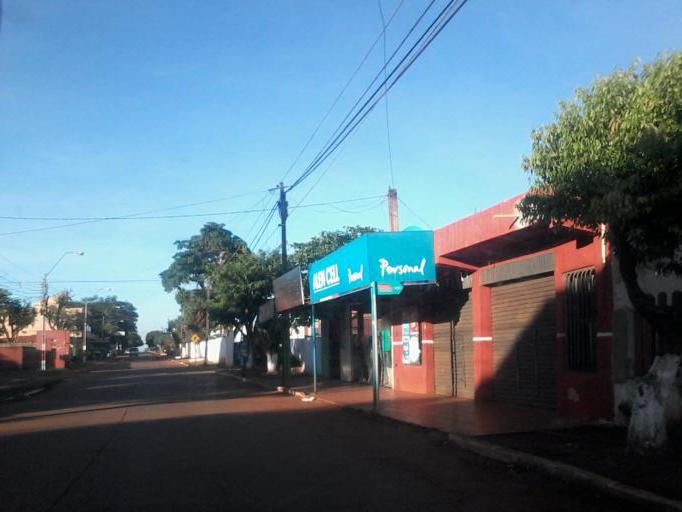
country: PY
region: Alto Parana
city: Ciudad del Este
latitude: -25.4354
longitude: -54.6401
